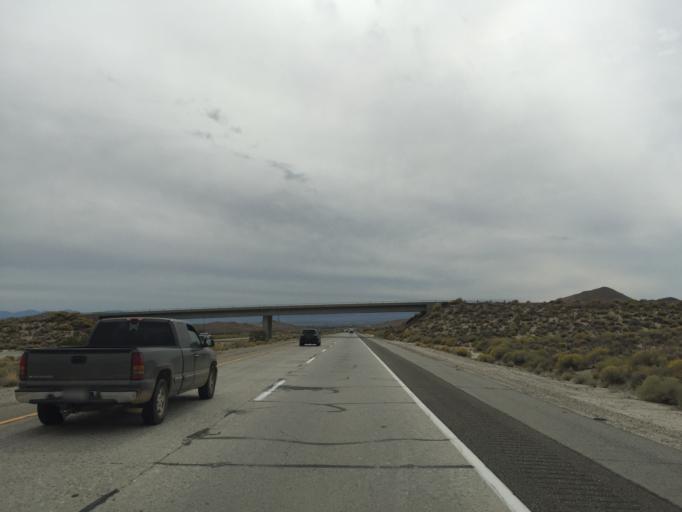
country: US
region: California
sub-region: Kern County
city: Rosamond
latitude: 34.9093
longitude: -118.1646
